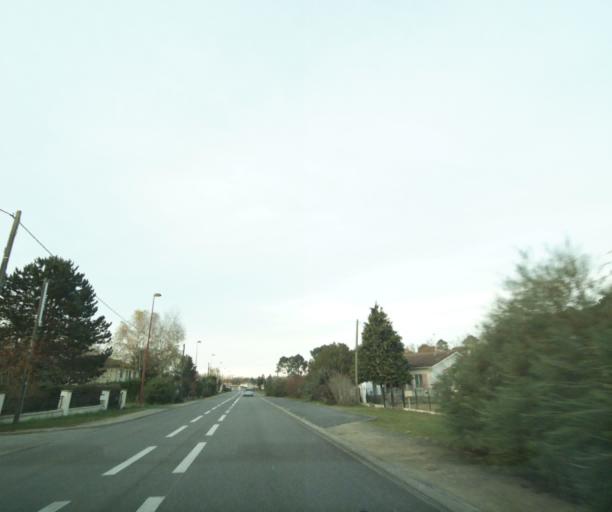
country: FR
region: Aquitaine
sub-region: Departement de la Gironde
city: Bazas
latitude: 44.3655
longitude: -0.2424
